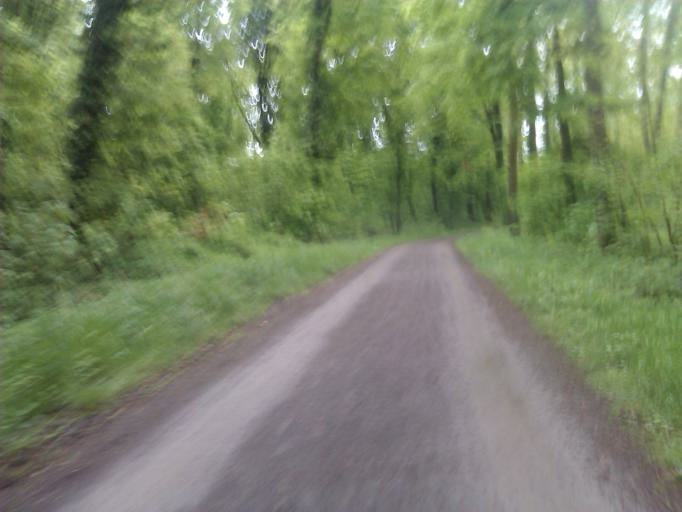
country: DE
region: Baden-Wuerttemberg
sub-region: Karlsruhe Region
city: Karlsruhe
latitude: 48.9832
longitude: 8.4206
